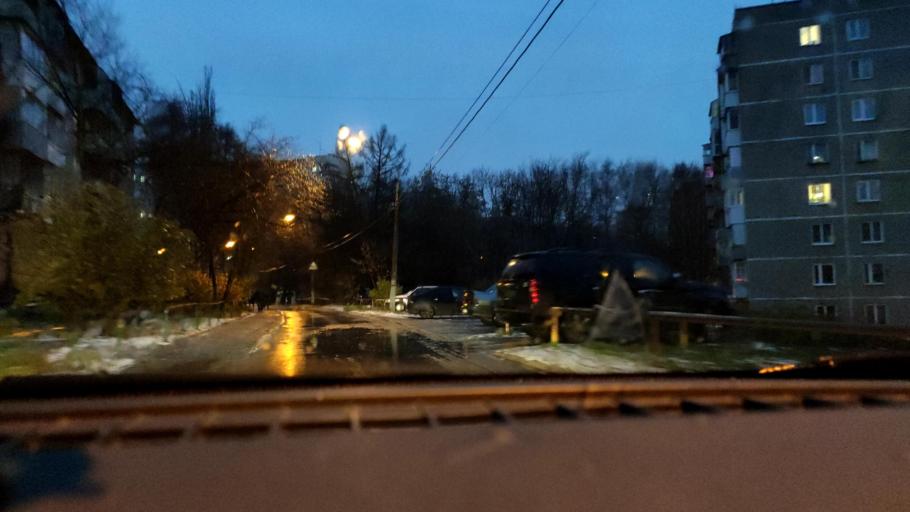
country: RU
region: Perm
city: Perm
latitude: 57.9818
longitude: 56.2240
